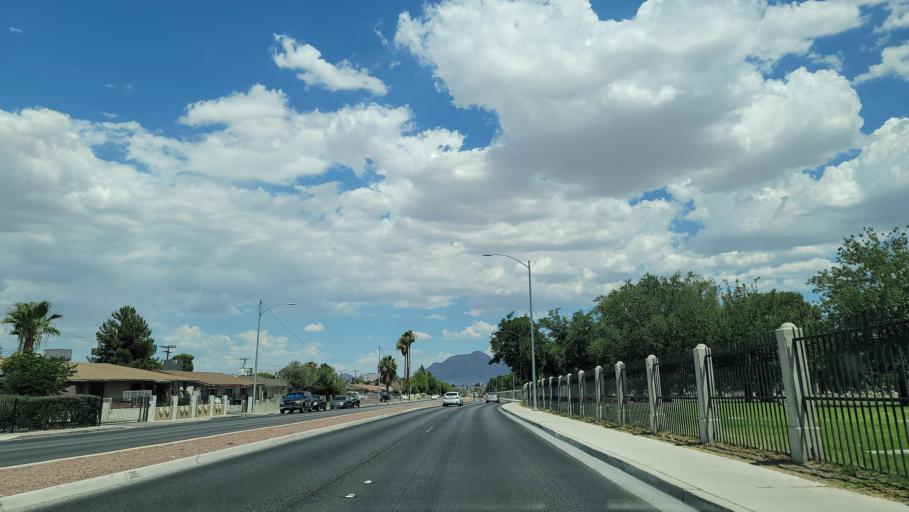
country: US
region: Nevada
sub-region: Clark County
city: Las Vegas
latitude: 36.1884
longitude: -115.1306
